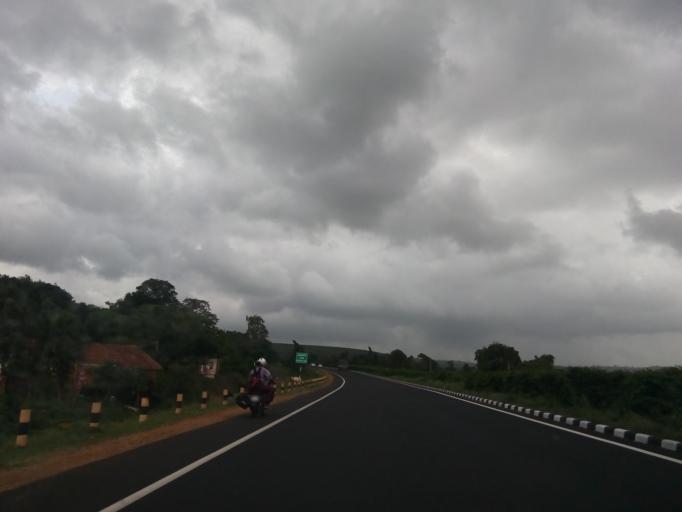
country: IN
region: Karnataka
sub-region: Belgaum
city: Hukeri
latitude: 16.0647
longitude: 74.5163
